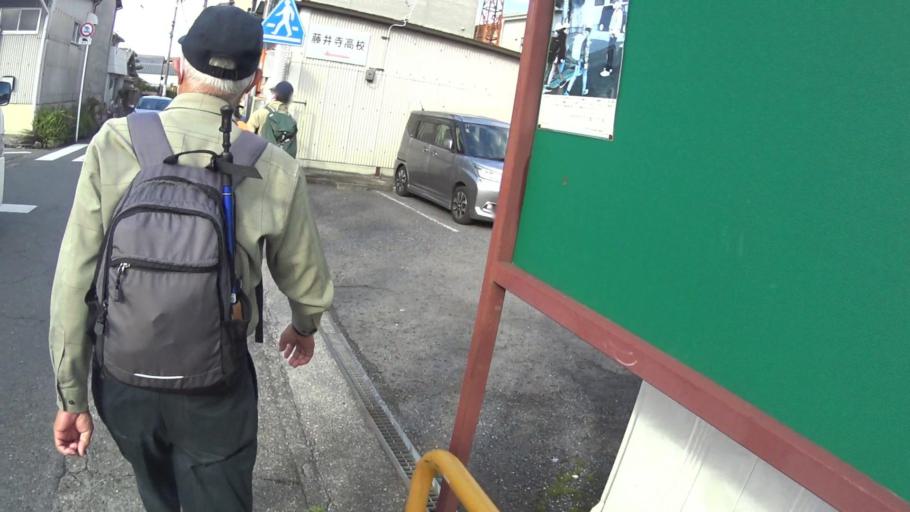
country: JP
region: Osaka
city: Kashihara
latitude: 34.5810
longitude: 135.5910
